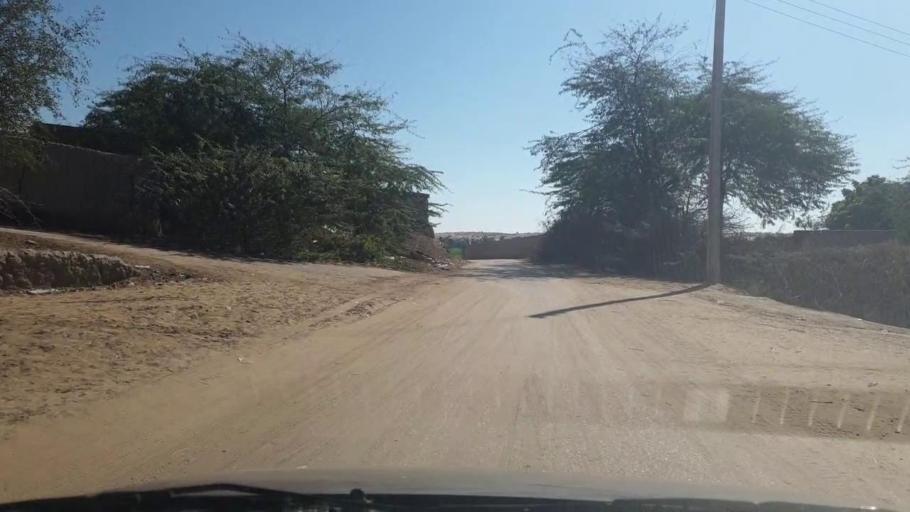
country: PK
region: Sindh
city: Bozdar
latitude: 27.0517
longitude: 68.6488
